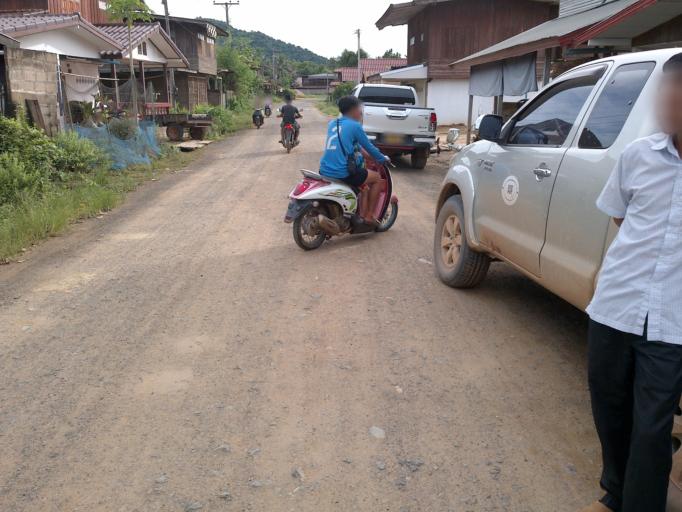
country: LA
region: Xiagnabouli
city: Muang Kenthao
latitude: 17.6903
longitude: 101.3765
